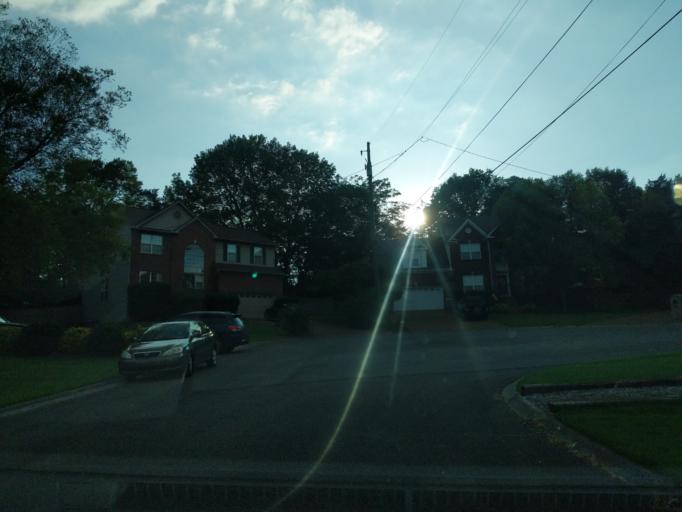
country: US
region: Tennessee
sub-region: Sumner County
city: Hendersonville
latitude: 36.2941
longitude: -86.6392
